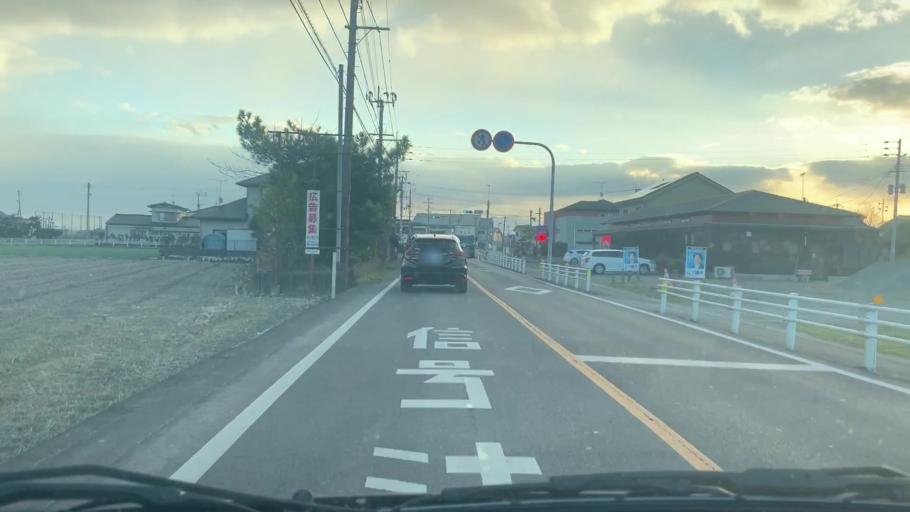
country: JP
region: Saga Prefecture
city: Saga-shi
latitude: 33.1864
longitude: 130.1928
